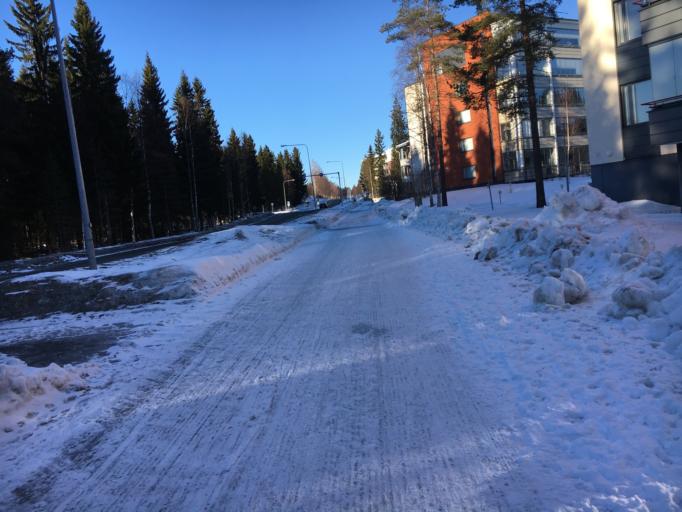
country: FI
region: Kainuu
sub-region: Kajaani
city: Kajaani
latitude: 64.2286
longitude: 27.7523
